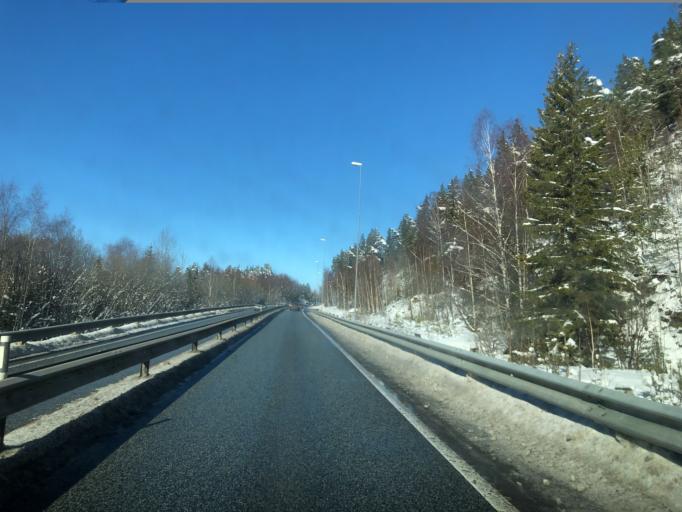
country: NO
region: Buskerud
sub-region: Hole
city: Vik
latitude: 60.0182
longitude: 10.2687
